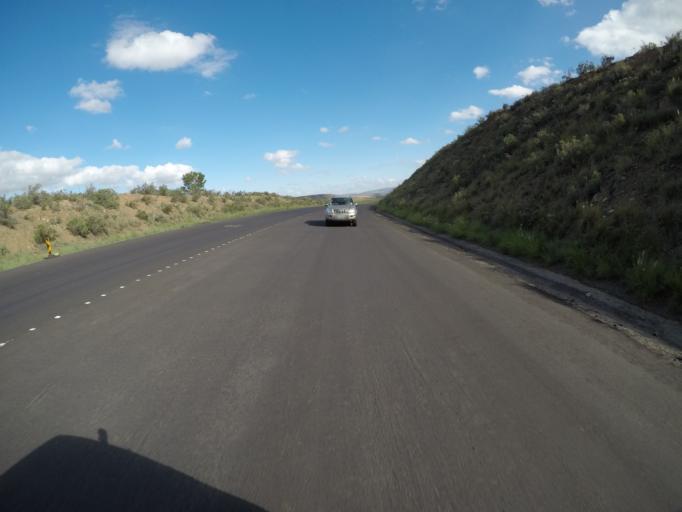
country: ZA
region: Western Cape
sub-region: Cape Winelands District Municipality
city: Ashton
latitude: -33.9411
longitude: 20.2152
